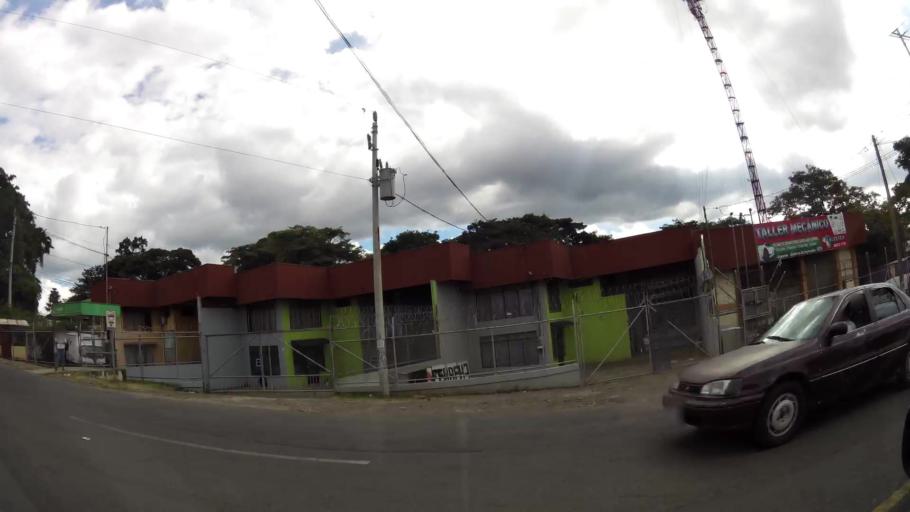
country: CR
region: San Jose
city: San Rafael
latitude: 9.9494
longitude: -84.1424
